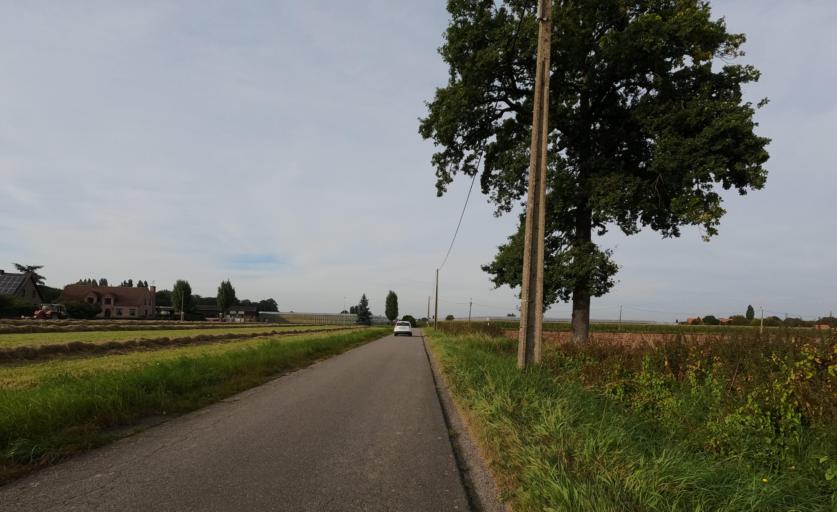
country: BE
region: Flanders
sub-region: Provincie Antwerpen
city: Wommelgem
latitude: 51.1843
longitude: 4.5117
